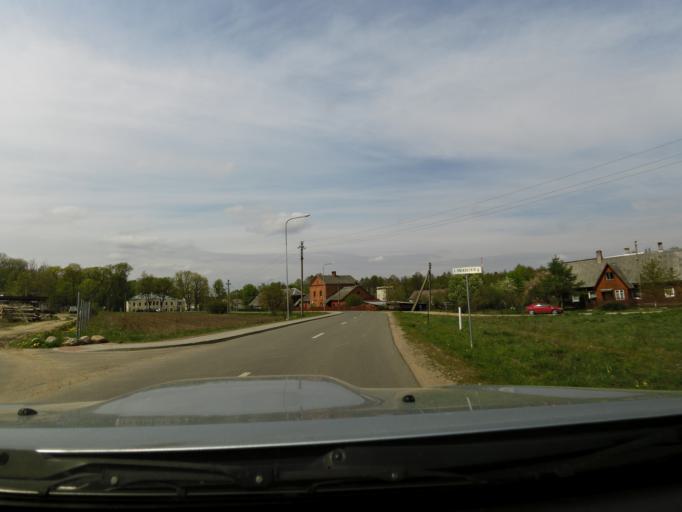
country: LT
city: Salcininkai
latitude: 54.4327
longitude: 25.3028
